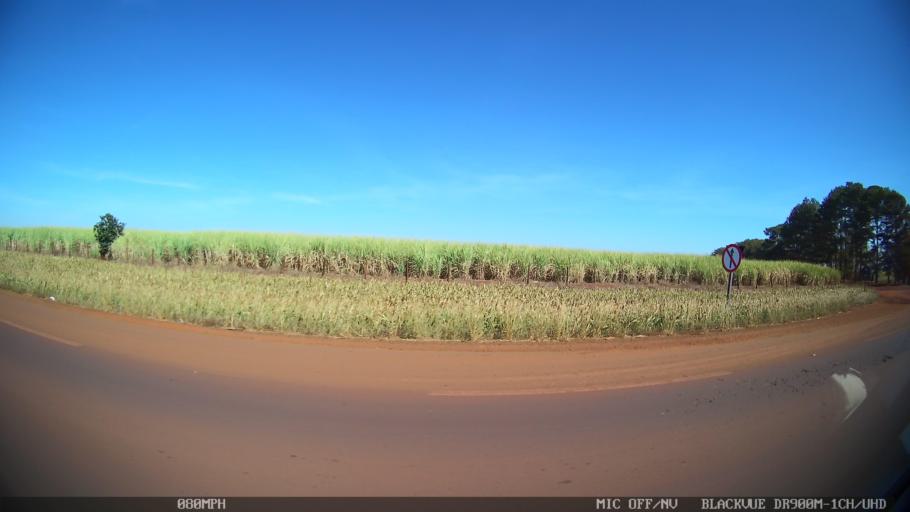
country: BR
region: Sao Paulo
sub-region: Ipua
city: Ipua
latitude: -20.4650
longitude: -48.1290
